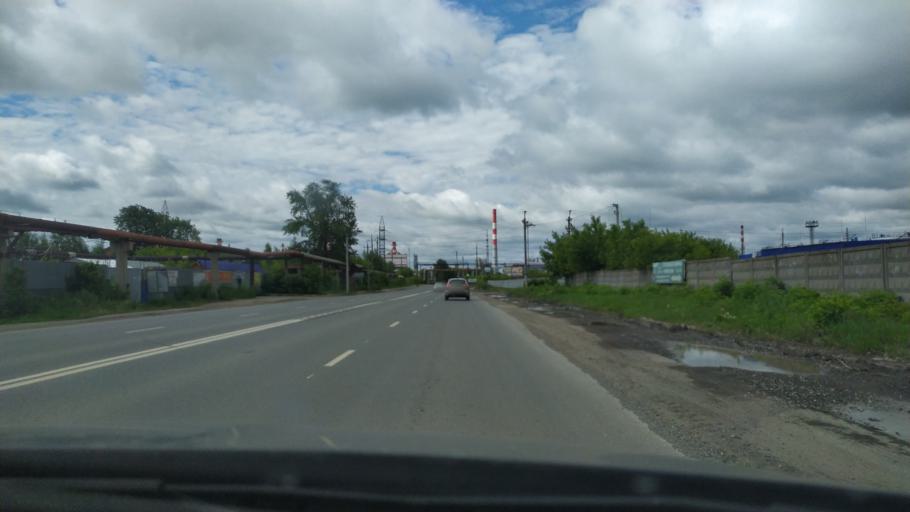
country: RU
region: Perm
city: Kondratovo
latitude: 57.9283
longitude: 56.1414
